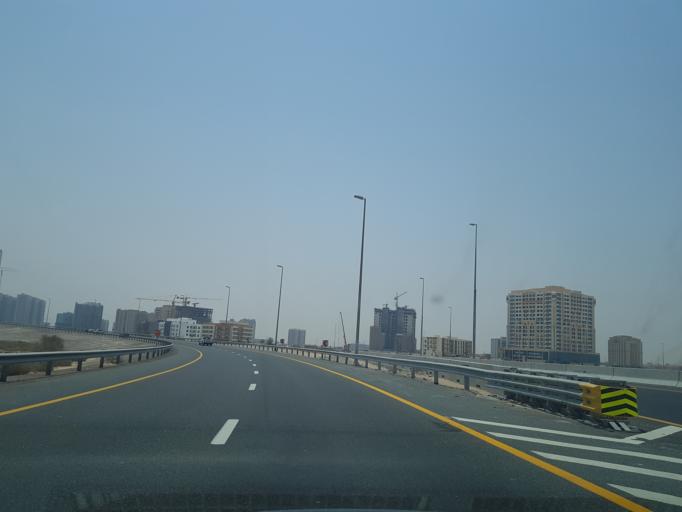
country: AE
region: Dubai
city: Dubai
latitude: 25.1039
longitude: 55.3752
